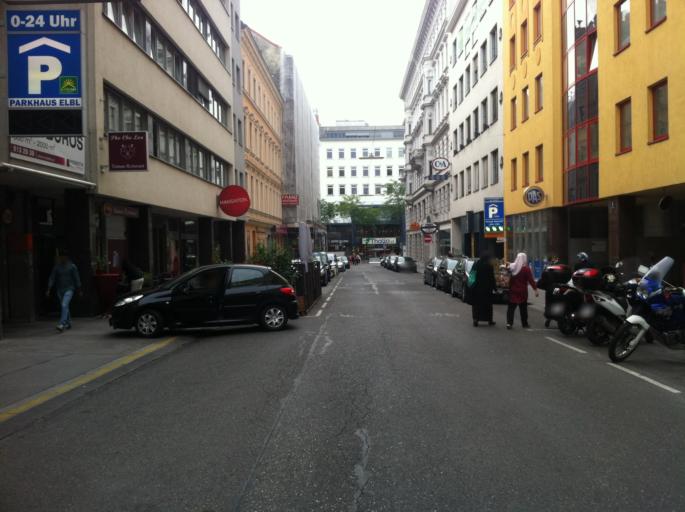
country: AT
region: Vienna
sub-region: Wien Stadt
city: Vienna
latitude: 48.1981
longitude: 16.3455
